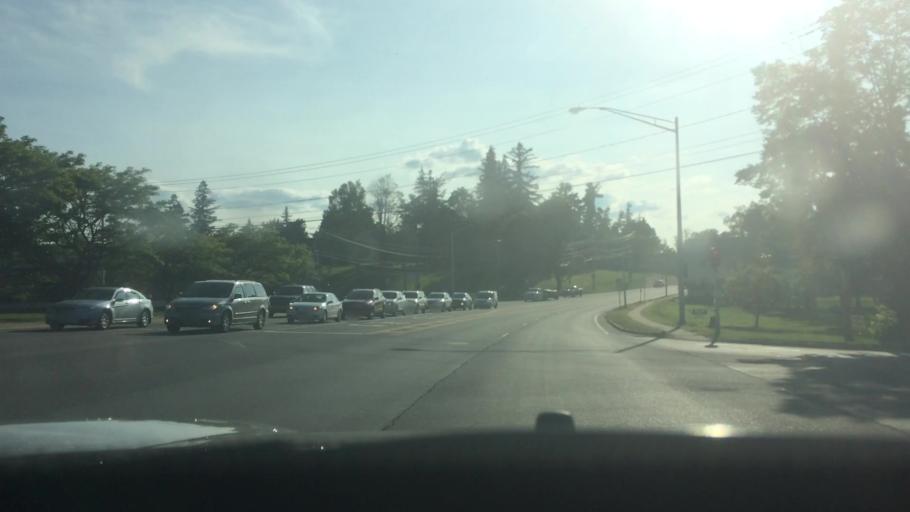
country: US
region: New York
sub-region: St. Lawrence County
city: Potsdam
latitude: 44.6677
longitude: -74.9944
